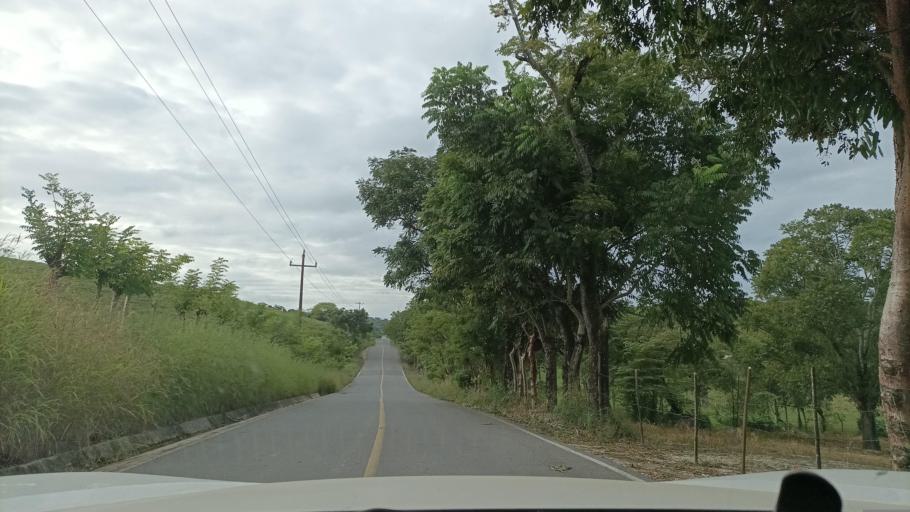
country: MX
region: Veracruz
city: Hidalgotitlan
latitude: 17.6963
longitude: -94.4689
